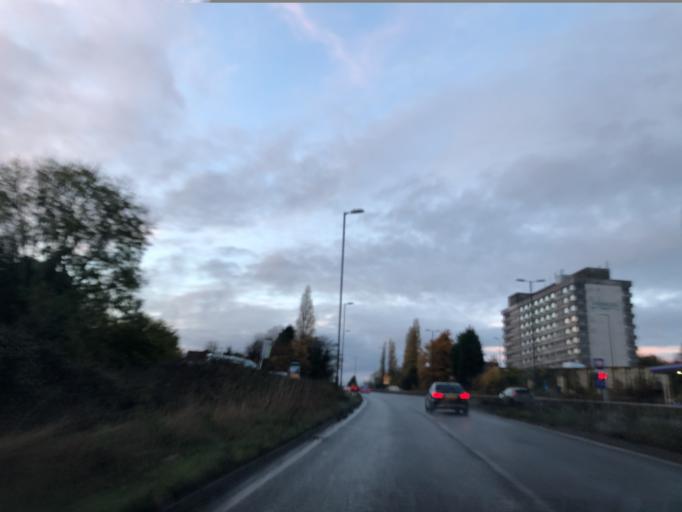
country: GB
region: England
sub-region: Coventry
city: Keresley
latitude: 52.4240
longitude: -1.5718
